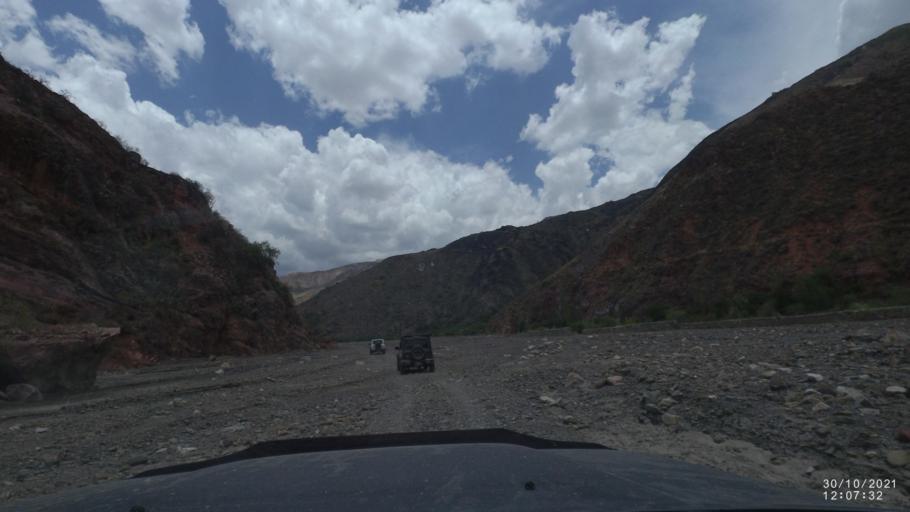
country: BO
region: Cochabamba
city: Colchani
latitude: -17.5396
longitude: -66.6261
